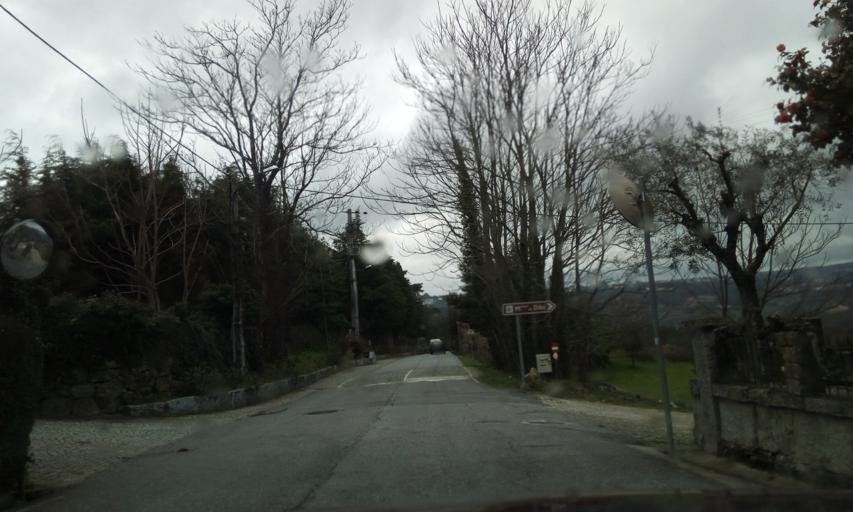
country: PT
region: Viseu
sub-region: Nelas
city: Nelas
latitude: 40.6027
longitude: -7.8452
